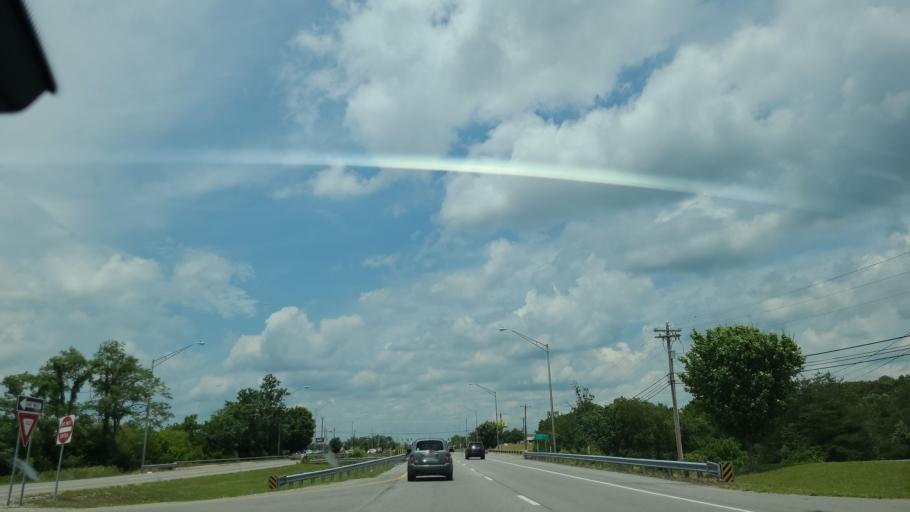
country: US
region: Tennessee
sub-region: Cumberland County
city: Crossville
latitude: 35.9751
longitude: -85.0382
